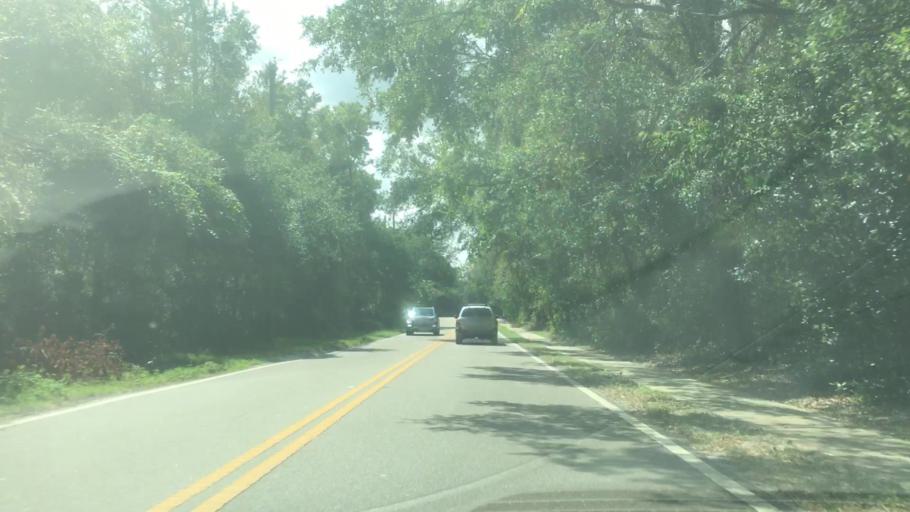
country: US
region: Florida
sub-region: Duval County
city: Jacksonville
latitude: 30.4476
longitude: -81.5792
